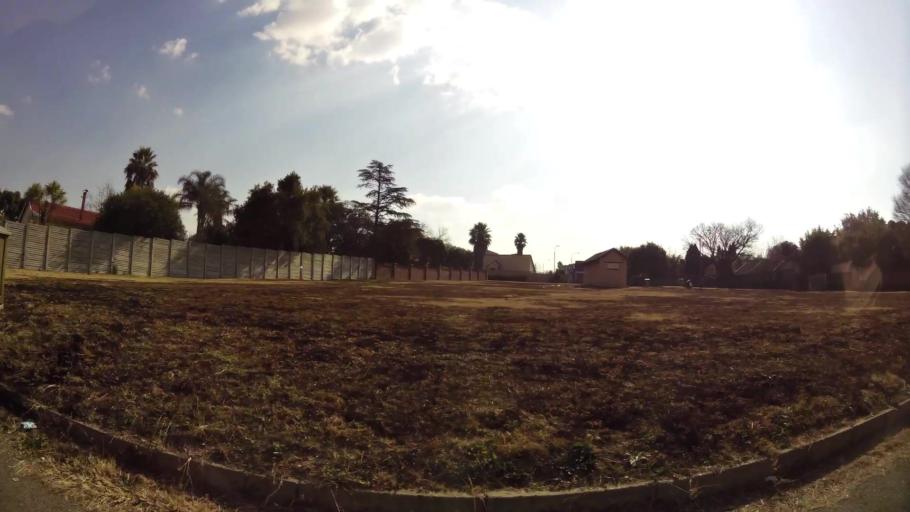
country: ZA
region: Gauteng
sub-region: City of Johannesburg Metropolitan Municipality
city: Modderfontein
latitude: -26.0964
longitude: 28.2147
